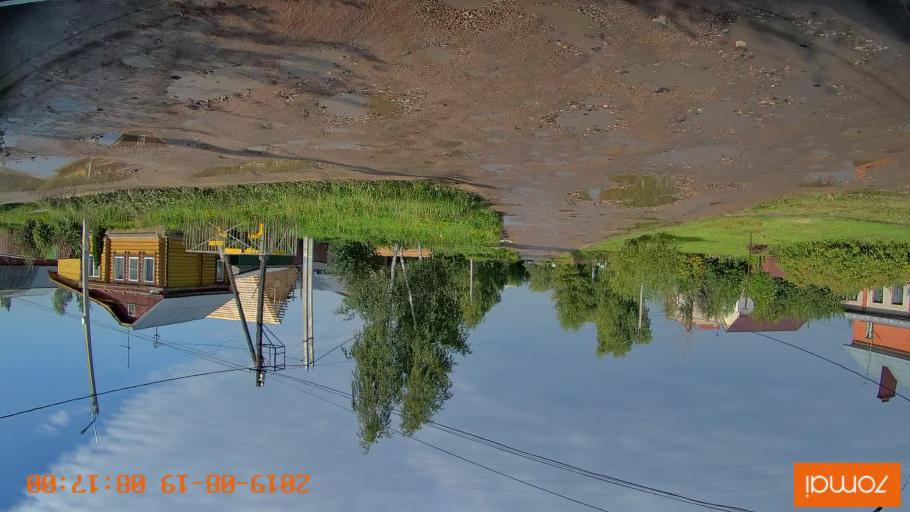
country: RU
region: Ivanovo
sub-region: Gorod Ivanovo
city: Ivanovo
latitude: 56.9755
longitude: 40.9982
